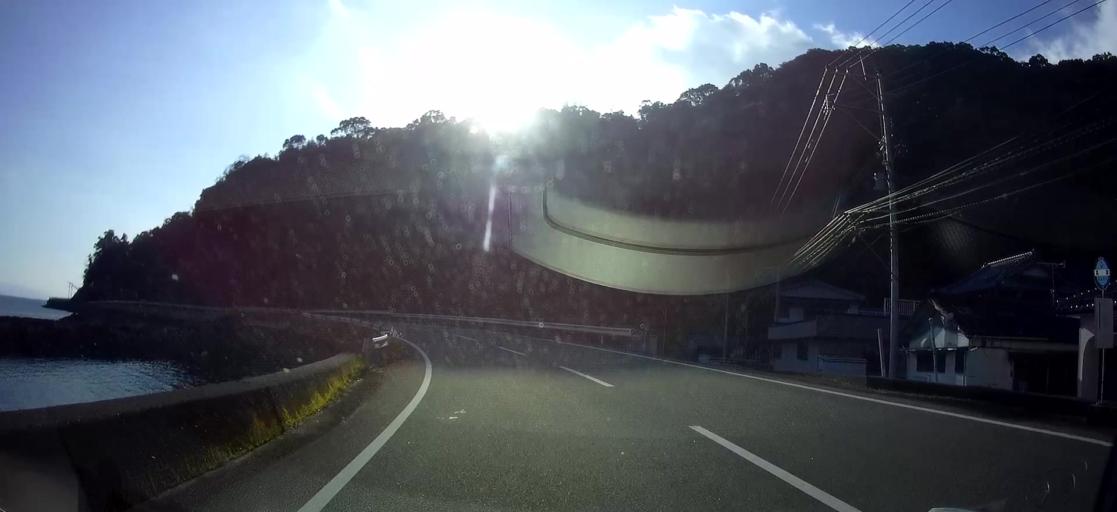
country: JP
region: Kumamoto
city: Minamata
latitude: 32.3873
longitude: 130.3820
